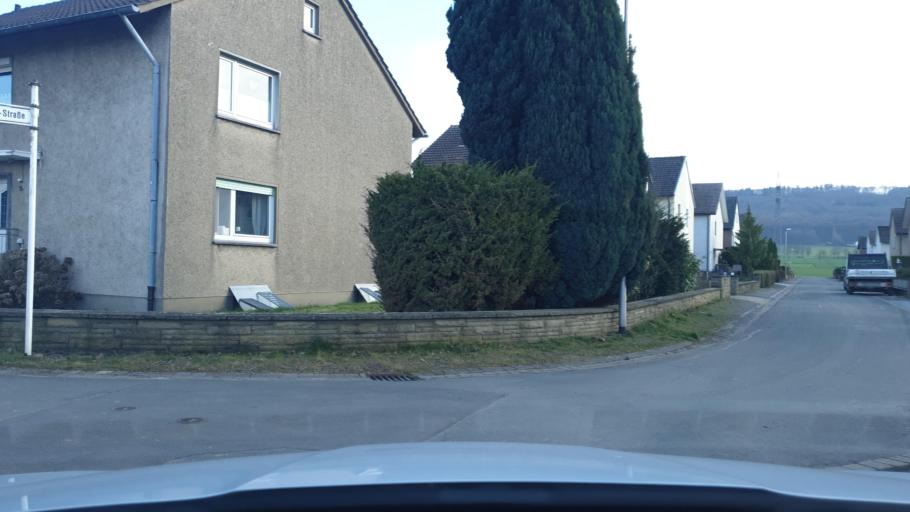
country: DE
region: North Rhine-Westphalia
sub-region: Regierungsbezirk Detmold
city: Minden
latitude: 52.2699
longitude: 8.8578
